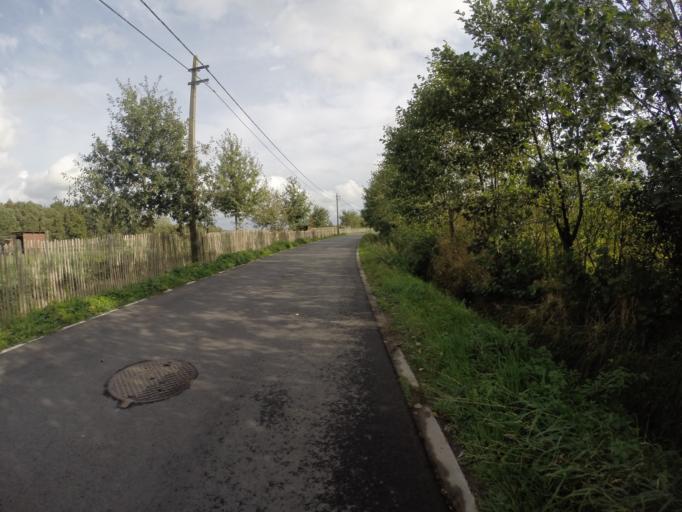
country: BE
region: Flanders
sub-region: Provincie West-Vlaanderen
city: Ruiselede
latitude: 51.0795
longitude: 3.4036
